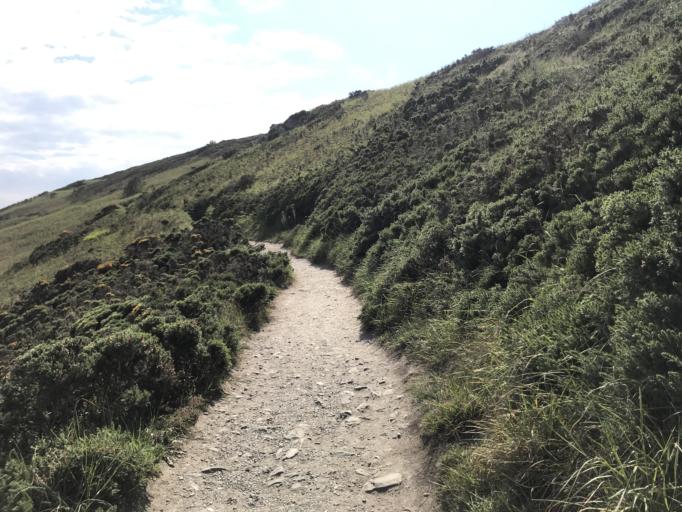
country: IE
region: Leinster
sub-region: Fingal County
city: Howth
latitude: 53.3729
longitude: -6.0497
